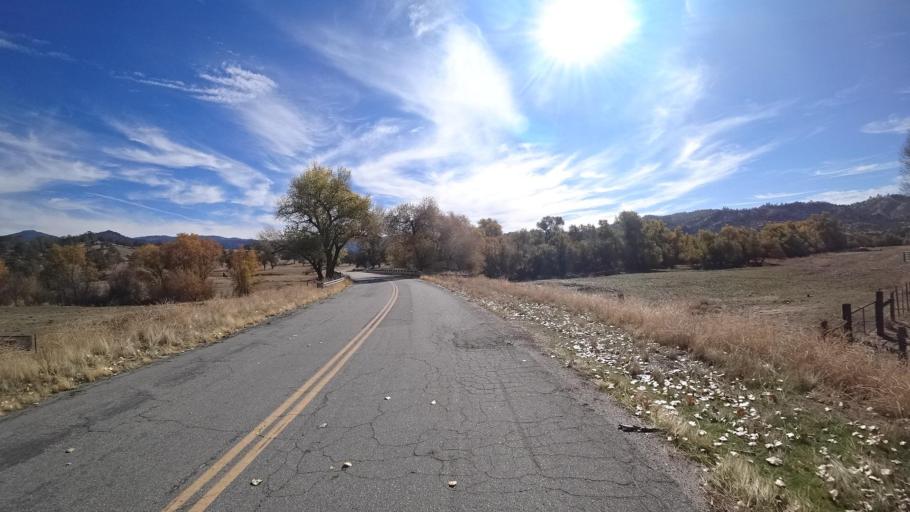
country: US
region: California
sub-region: Kern County
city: Alta Sierra
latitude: 35.6274
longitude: -118.7496
